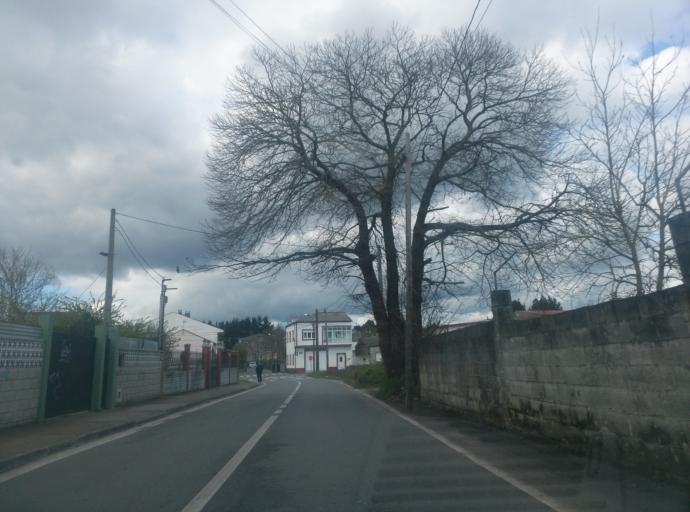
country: ES
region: Galicia
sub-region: Provincia de Lugo
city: Lugo
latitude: 43.0262
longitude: -7.5535
